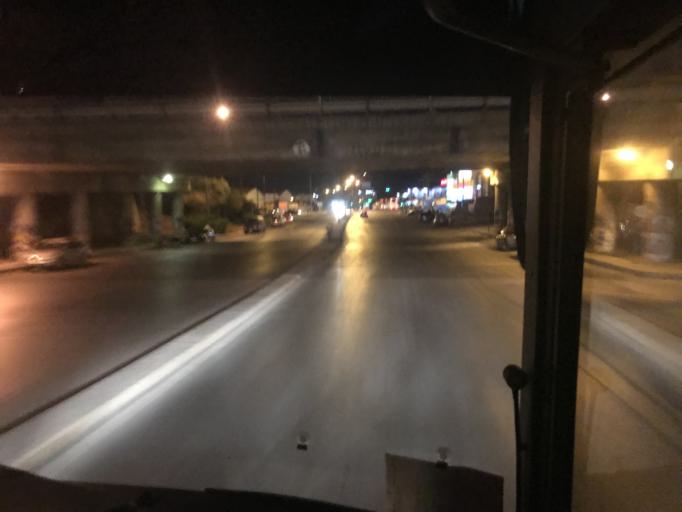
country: GR
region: Crete
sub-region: Nomos Irakleiou
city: Nea Alikarnassos
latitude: 35.3321
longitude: 25.1592
